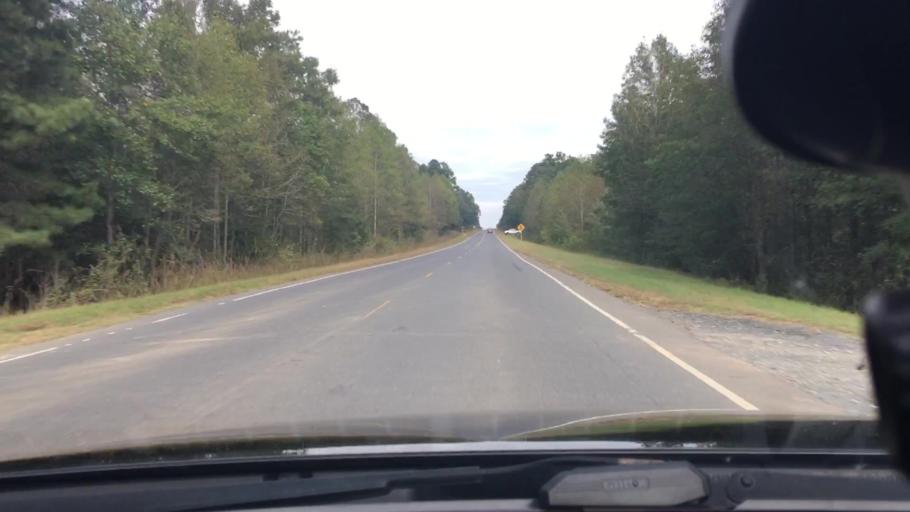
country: US
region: North Carolina
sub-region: Montgomery County
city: Troy
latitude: 35.3160
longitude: -79.9788
